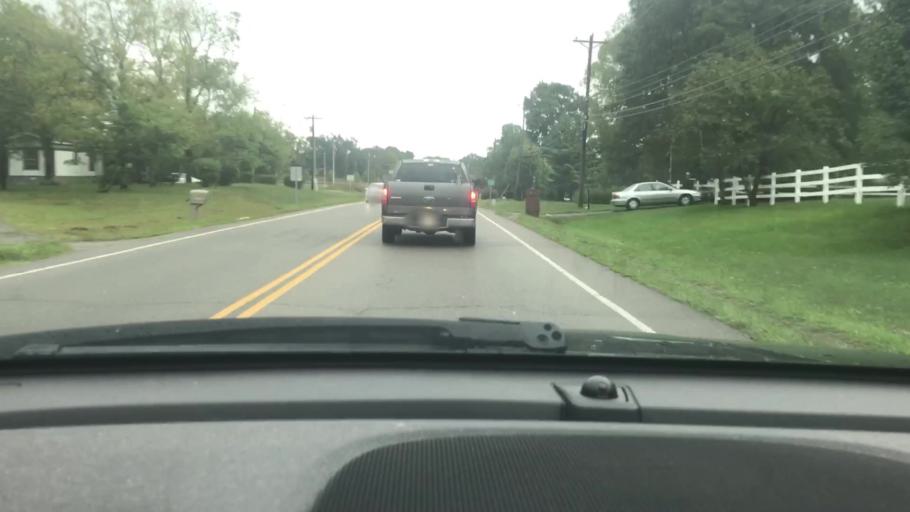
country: US
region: Tennessee
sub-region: Dickson County
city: White Bluff
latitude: 36.1049
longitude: -87.1909
